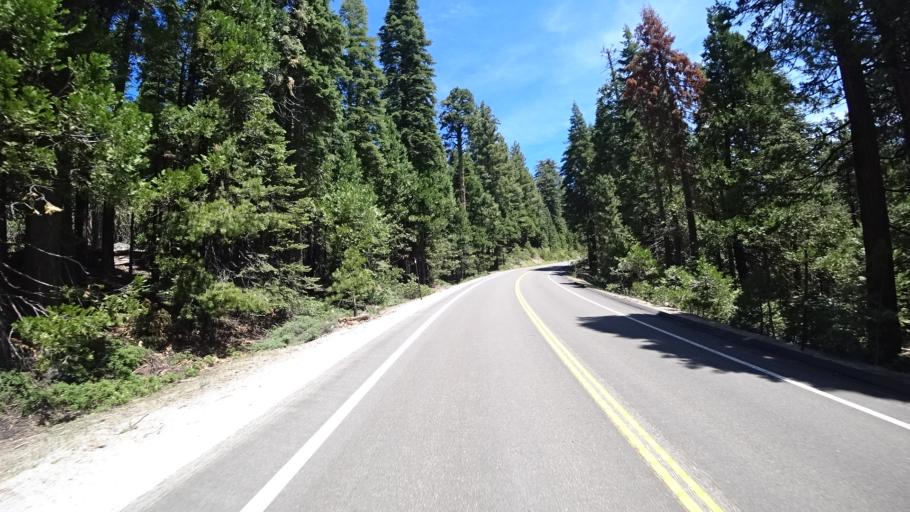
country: US
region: California
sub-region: Calaveras County
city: Arnold
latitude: 38.3579
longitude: -120.2120
